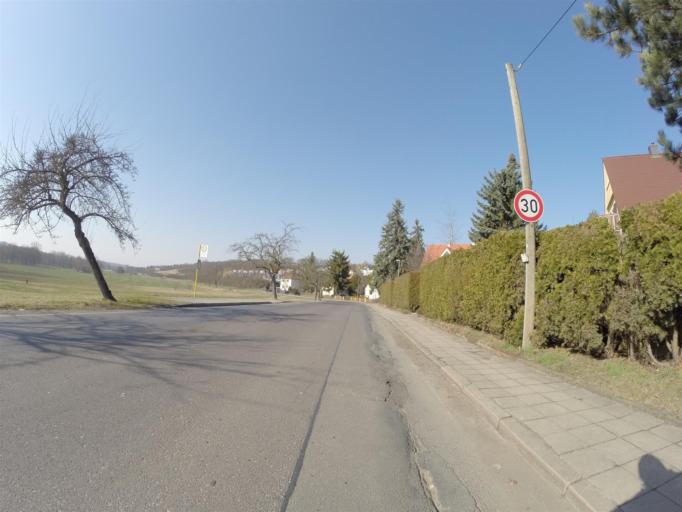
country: DE
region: Thuringia
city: Mellingen
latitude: 50.9520
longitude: 11.3751
